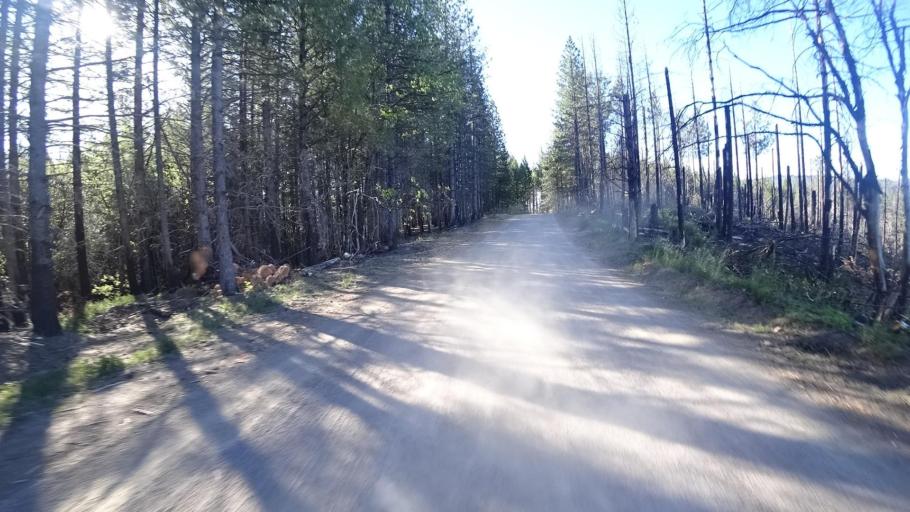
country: US
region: California
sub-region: Lake County
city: Upper Lake
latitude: 39.3476
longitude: -122.9708
